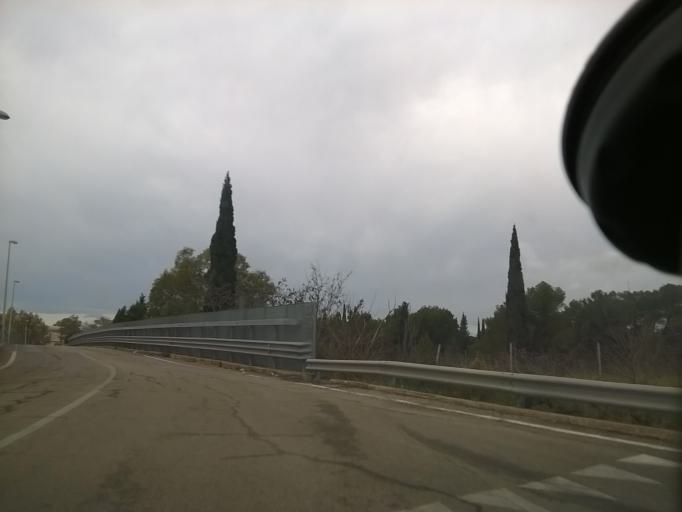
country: IT
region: Apulia
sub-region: Provincia di Taranto
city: Paolo VI
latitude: 40.5038
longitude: 17.2665
